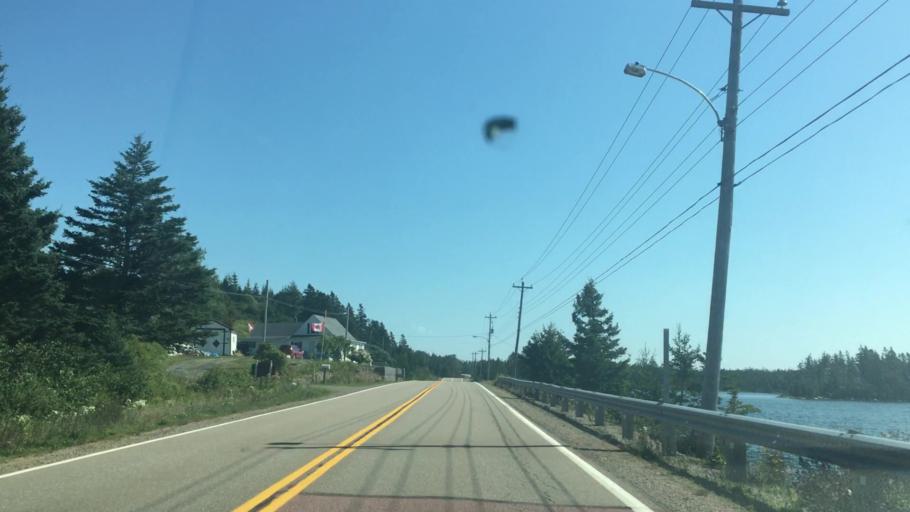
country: CA
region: Nova Scotia
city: Antigonish
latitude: 45.0227
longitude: -62.0168
